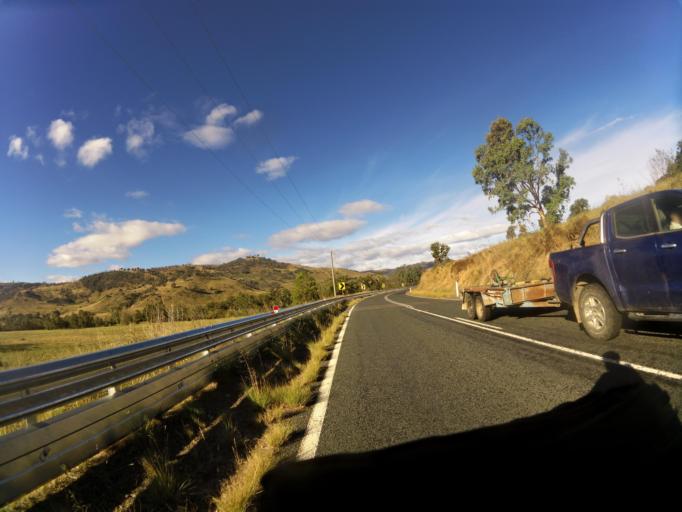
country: AU
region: New South Wales
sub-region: Greater Hume Shire
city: Holbrook
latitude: -35.9652
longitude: 147.7635
